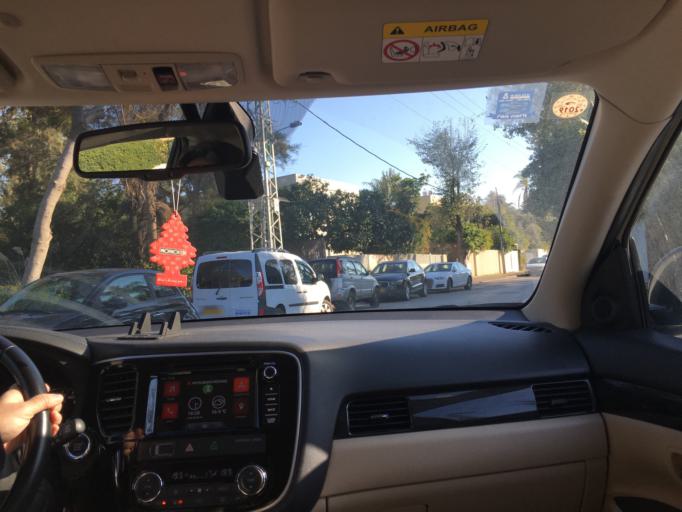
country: IL
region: Tel Aviv
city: Ramat HaSharon
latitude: 32.1504
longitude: 34.8335
